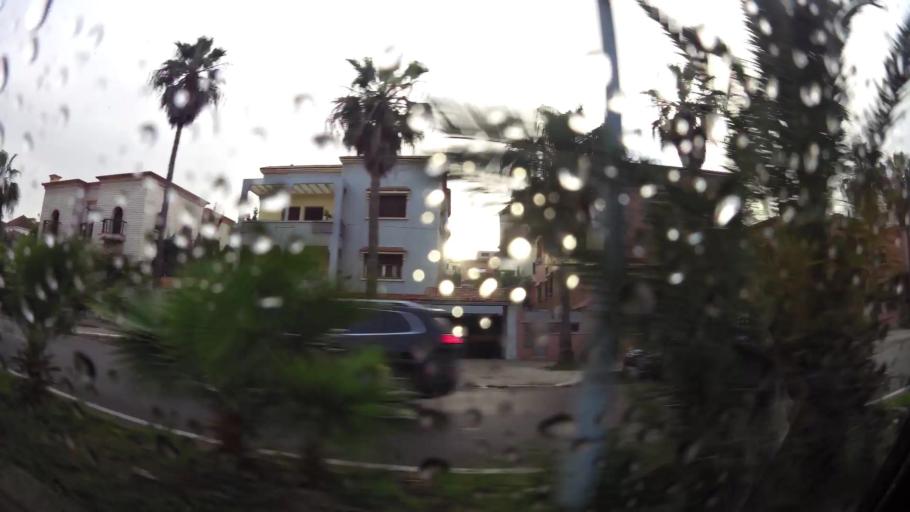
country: MA
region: Doukkala-Abda
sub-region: El-Jadida
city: El Jadida
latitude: 33.2308
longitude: -8.4933
